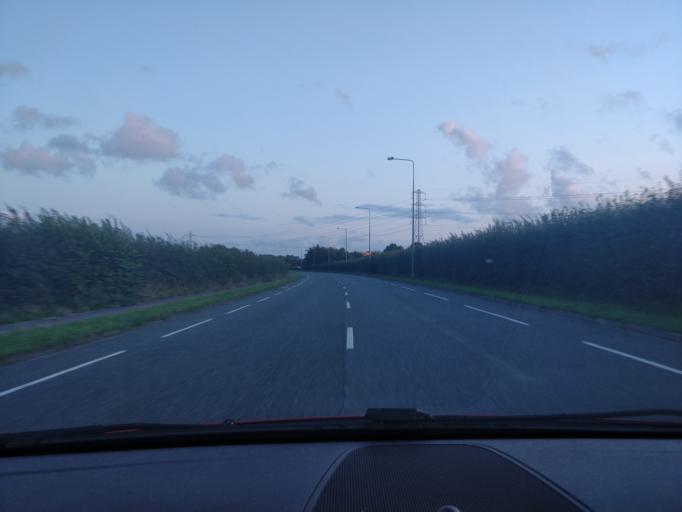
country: GB
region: England
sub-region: Lancashire
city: Tarleton
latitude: 53.6908
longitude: -2.8152
